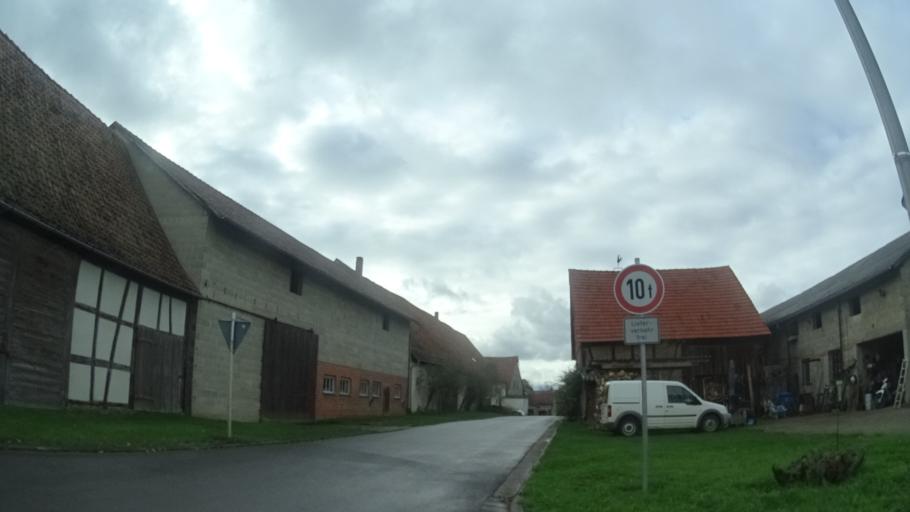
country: DE
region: Bavaria
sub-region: Regierungsbezirk Unterfranken
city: Hochheim
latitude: 50.3648
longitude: 10.4707
